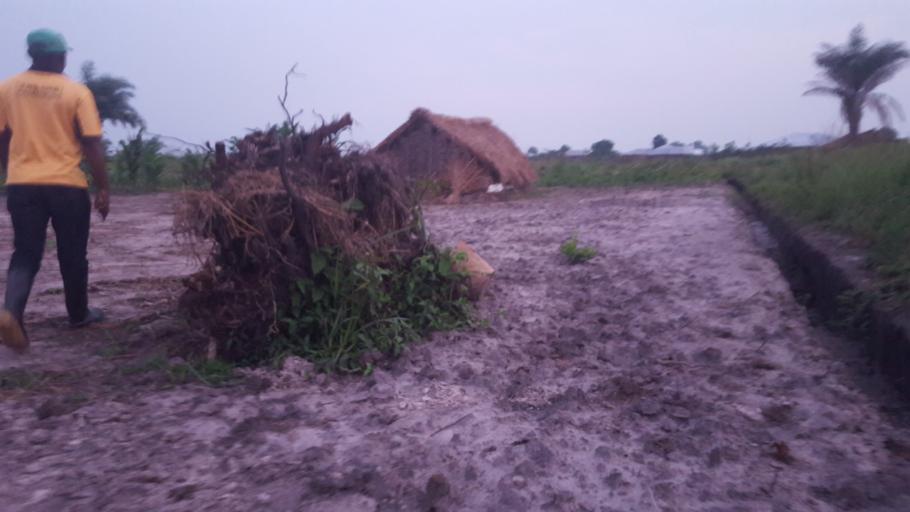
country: CD
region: Bandundu
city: Bandundu
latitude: -3.2801
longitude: 17.3851
